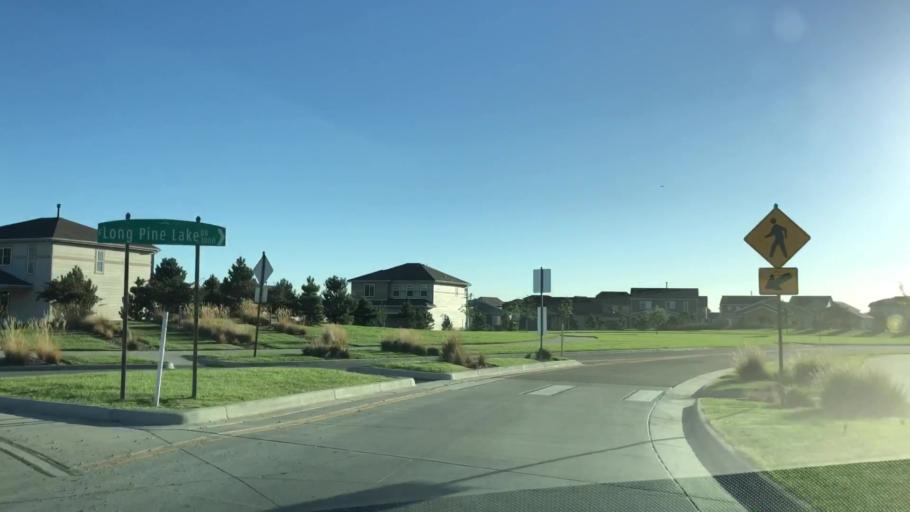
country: US
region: Colorado
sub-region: Larimer County
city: Loveland
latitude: 40.4193
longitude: -105.0206
